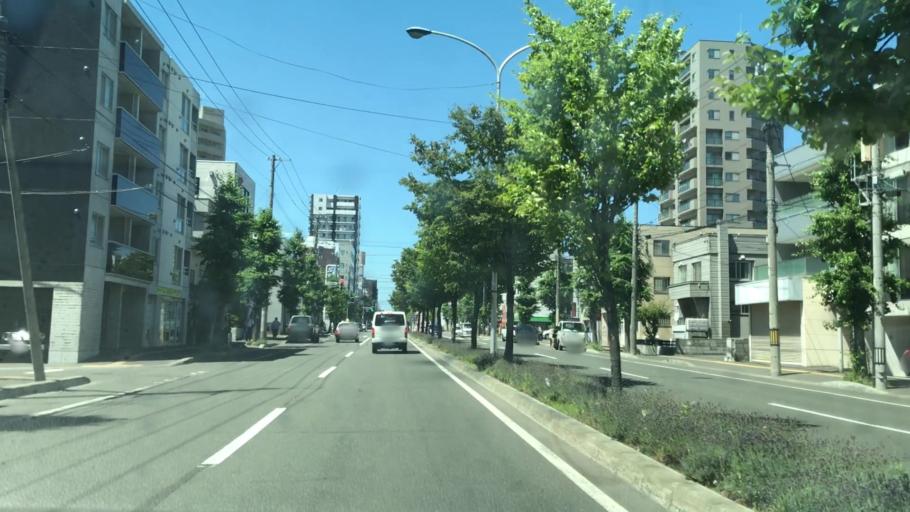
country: JP
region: Hokkaido
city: Sapporo
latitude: 43.0737
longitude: 141.3073
